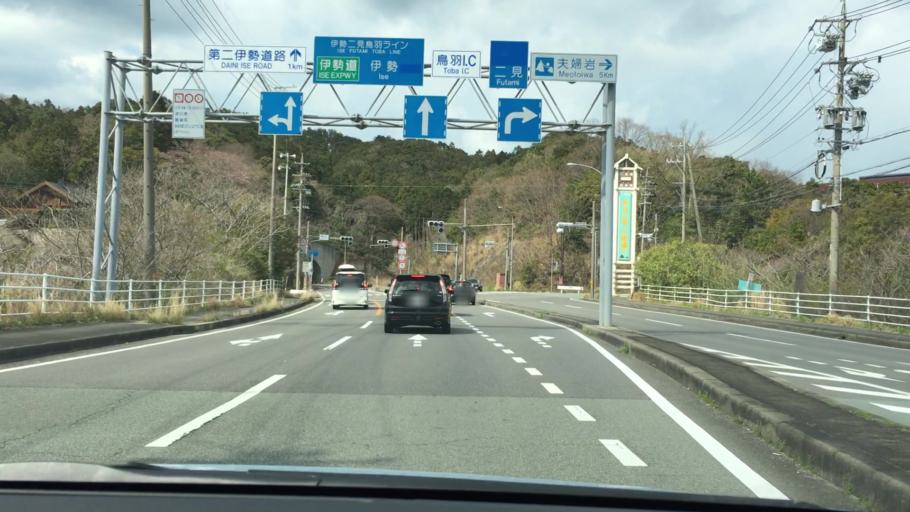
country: JP
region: Mie
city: Toba
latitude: 34.4853
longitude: 136.8158
